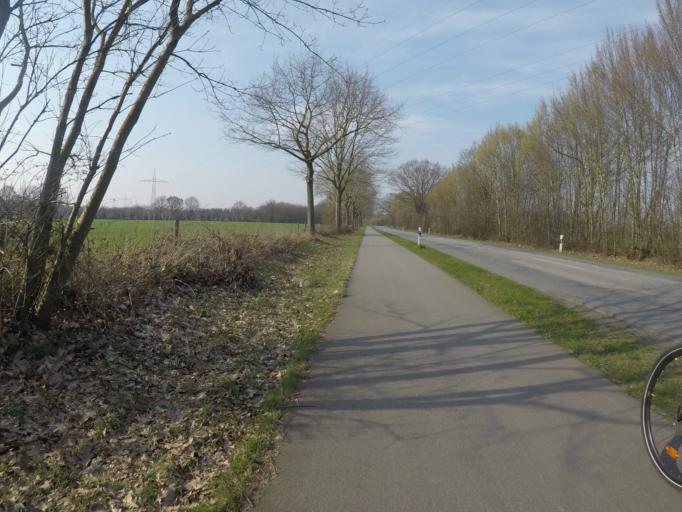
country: DE
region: Schleswig-Holstein
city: Wittenborn
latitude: 53.9375
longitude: 10.2240
